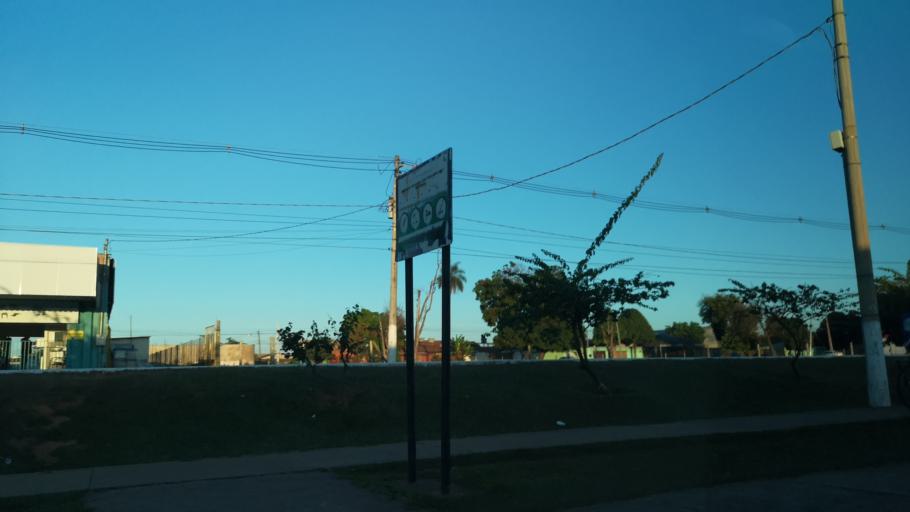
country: BR
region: Goias
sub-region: Senador Canedo
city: Senador Canedo
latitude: -16.6892
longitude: -49.1095
